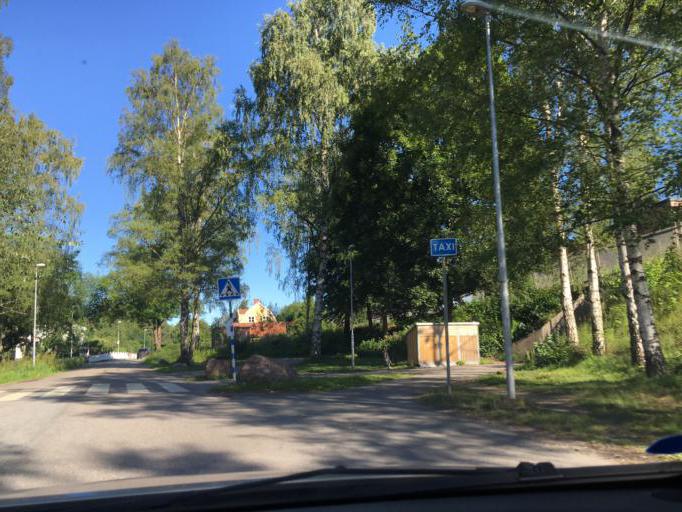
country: SE
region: Stockholm
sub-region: Sodertalje Kommun
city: Pershagen
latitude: 59.1838
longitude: 17.6607
